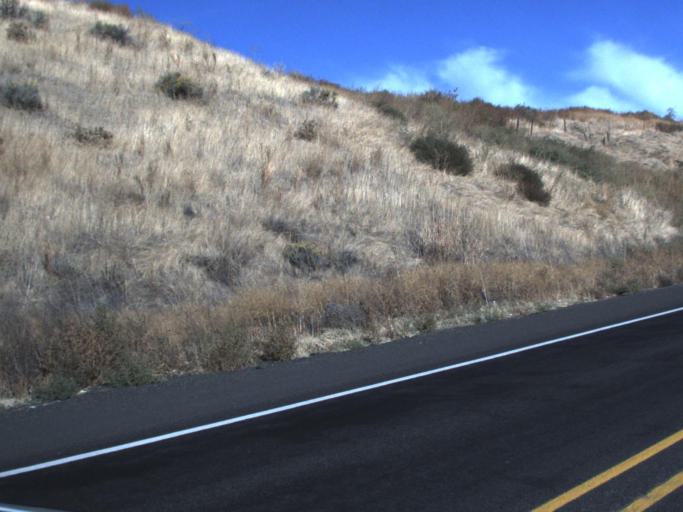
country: US
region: Washington
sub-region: Franklin County
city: Basin City
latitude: 46.5925
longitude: -119.0069
